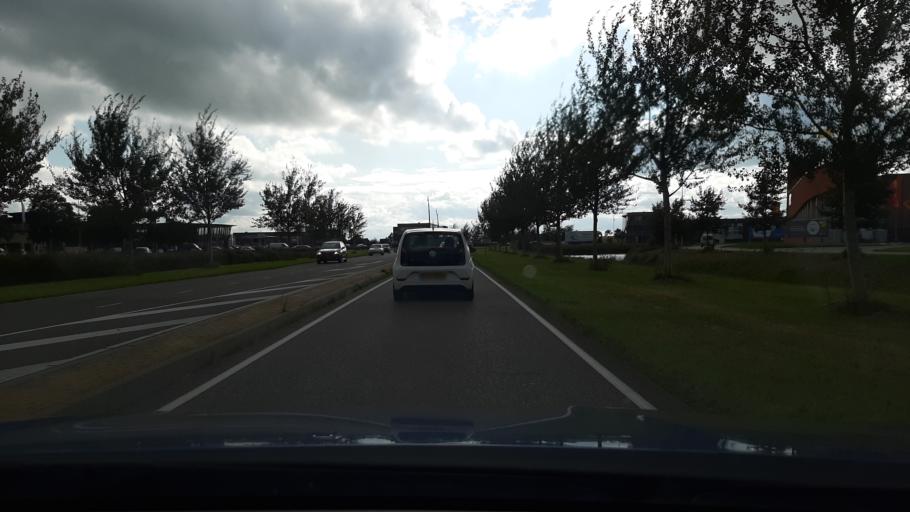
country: NL
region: Friesland
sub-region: Sudwest Fryslan
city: IJlst
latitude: 53.0364
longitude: 5.6285
